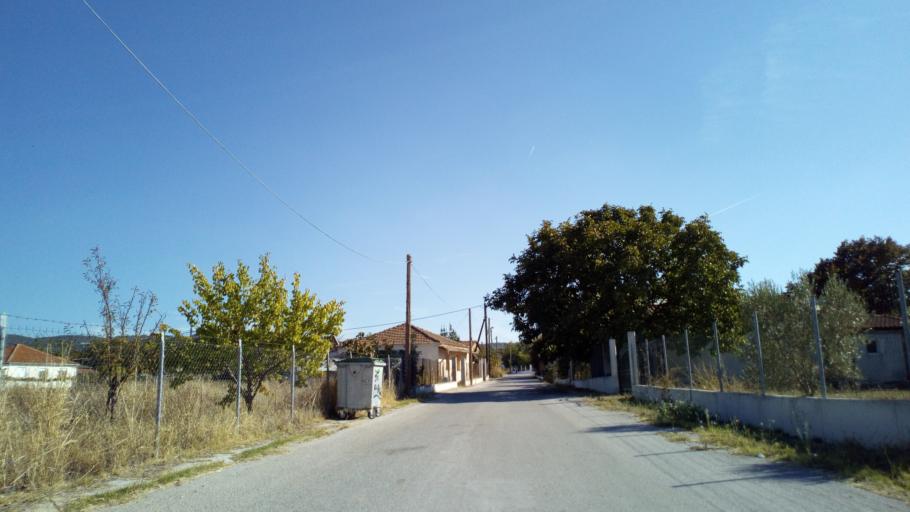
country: GR
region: Central Macedonia
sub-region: Nomos Thessalonikis
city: Gerakarou
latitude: 40.6373
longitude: 23.2501
